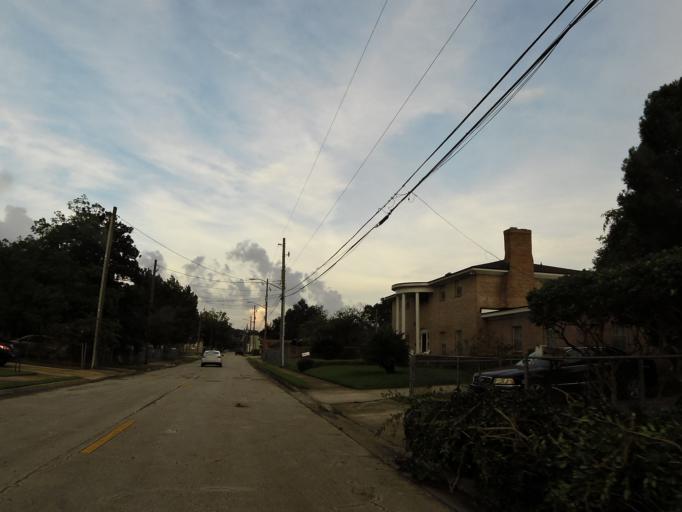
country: US
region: Florida
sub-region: Duval County
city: Jacksonville
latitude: 30.3486
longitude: -81.6997
